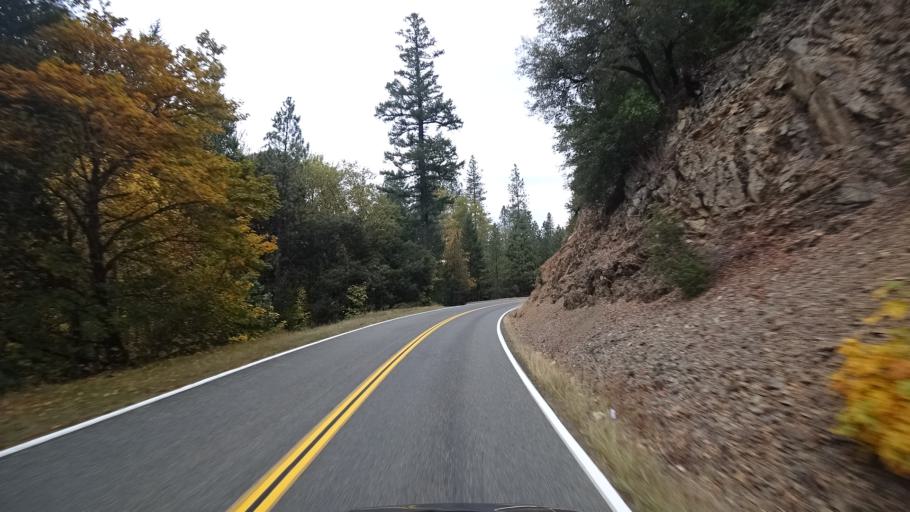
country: US
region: California
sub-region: Siskiyou County
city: Happy Camp
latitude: 41.8920
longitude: -123.4335
